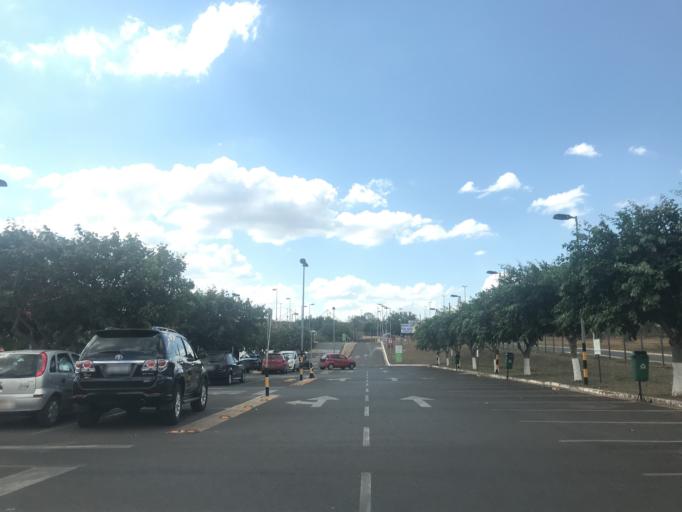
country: BR
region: Federal District
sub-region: Brasilia
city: Brasilia
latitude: -15.8354
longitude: -47.9497
